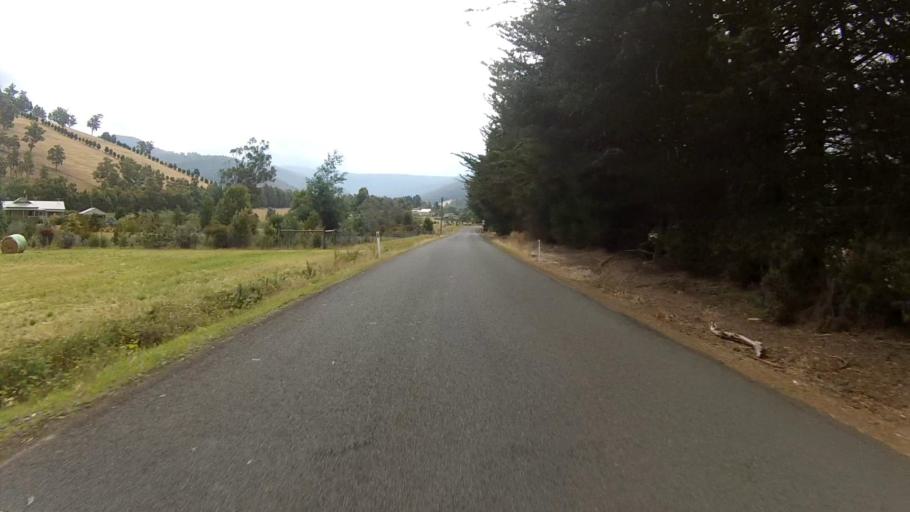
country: AU
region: Tasmania
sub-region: Huon Valley
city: Huonville
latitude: -42.9858
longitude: 147.0592
